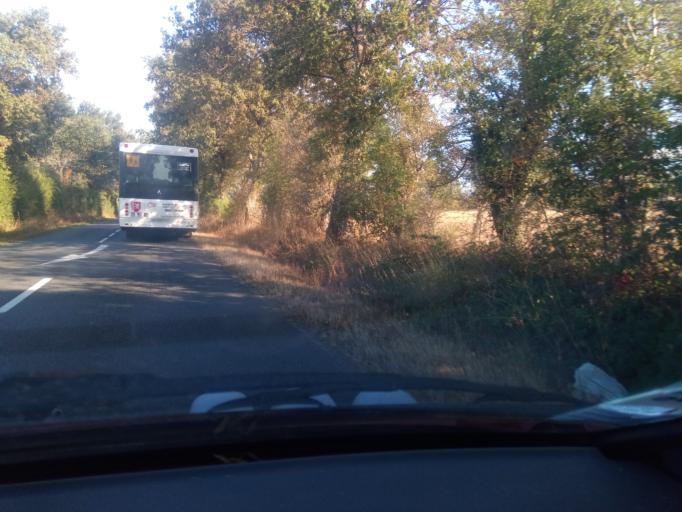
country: FR
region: Poitou-Charentes
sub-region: Departement de la Vienne
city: Availles-Limouzine
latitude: 46.1899
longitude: 0.7216
